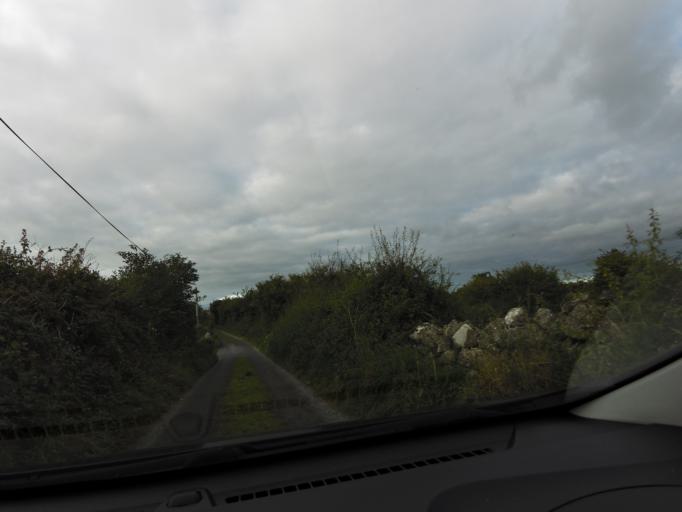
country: IE
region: Connaught
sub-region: County Galway
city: Ballinasloe
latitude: 53.3561
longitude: -8.0940
